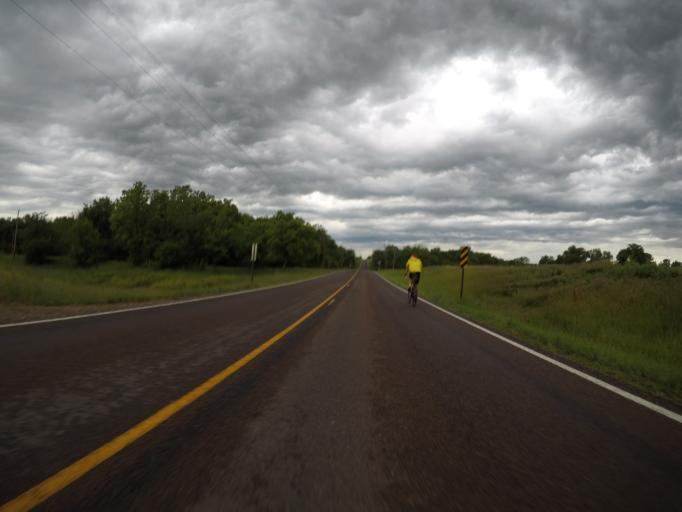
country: US
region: Kansas
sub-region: Shawnee County
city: Auburn
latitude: 38.9645
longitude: -95.9592
